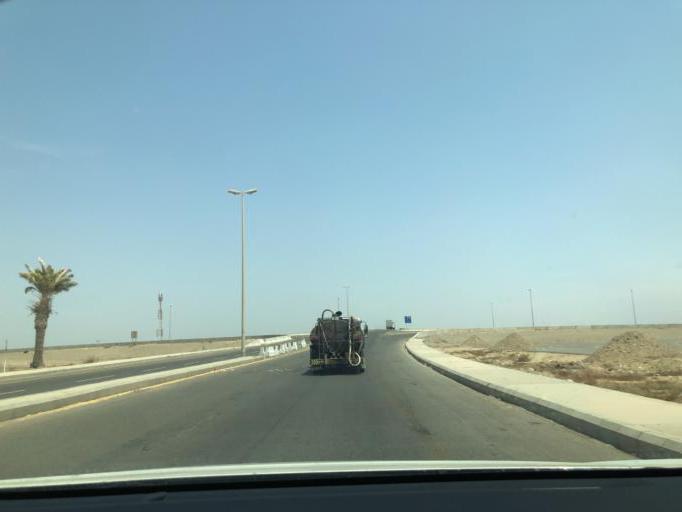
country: SA
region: Makkah
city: Rabigh
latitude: 22.2751
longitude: 39.1231
